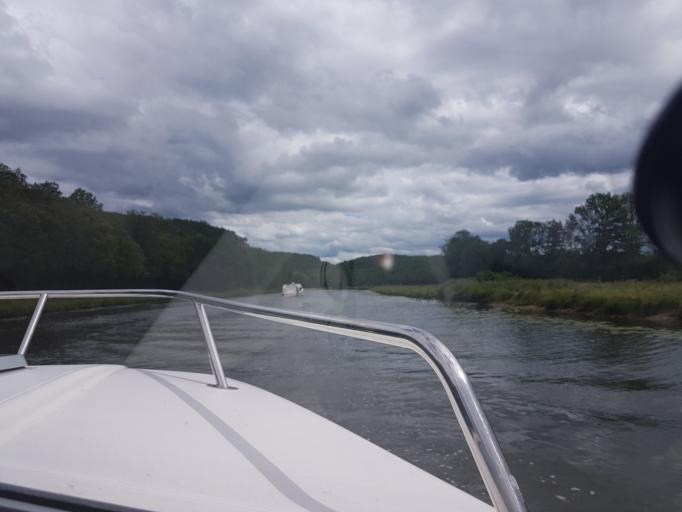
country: FR
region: Bourgogne
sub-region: Departement de l'Yonne
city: Vermenton
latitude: 47.5822
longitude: 3.6460
